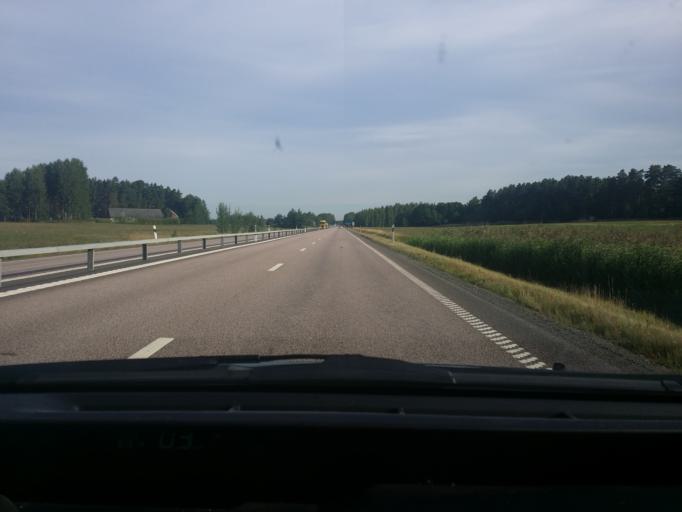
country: SE
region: Vaestmanland
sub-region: Vasteras
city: Hokasen
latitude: 59.6824
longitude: 16.5797
